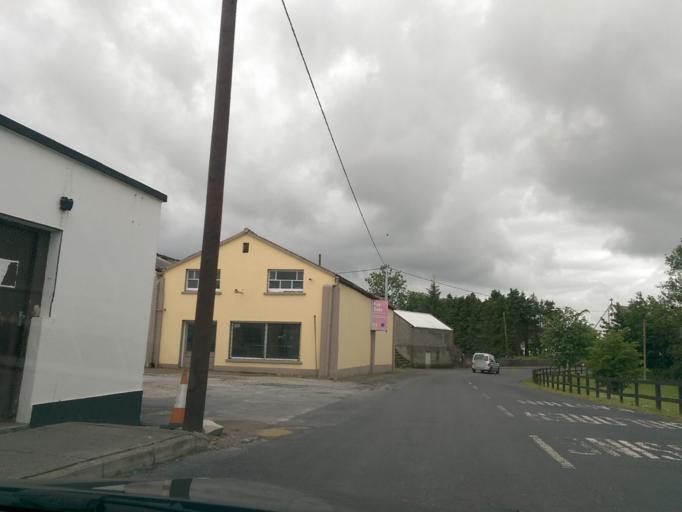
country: IE
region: Connaught
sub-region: County Galway
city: Loughrea
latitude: 53.3000
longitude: -8.4892
